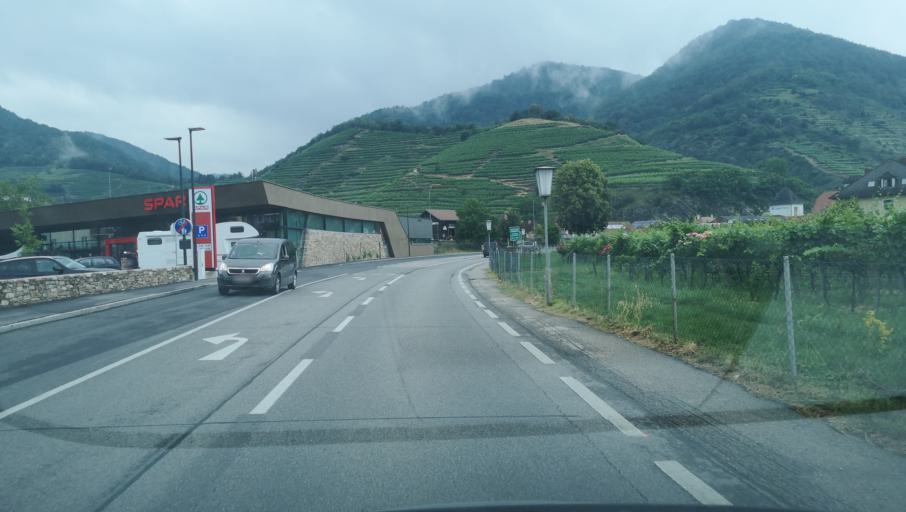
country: AT
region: Lower Austria
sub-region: Politischer Bezirk Krems
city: Spitz
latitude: 48.3639
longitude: 15.4176
